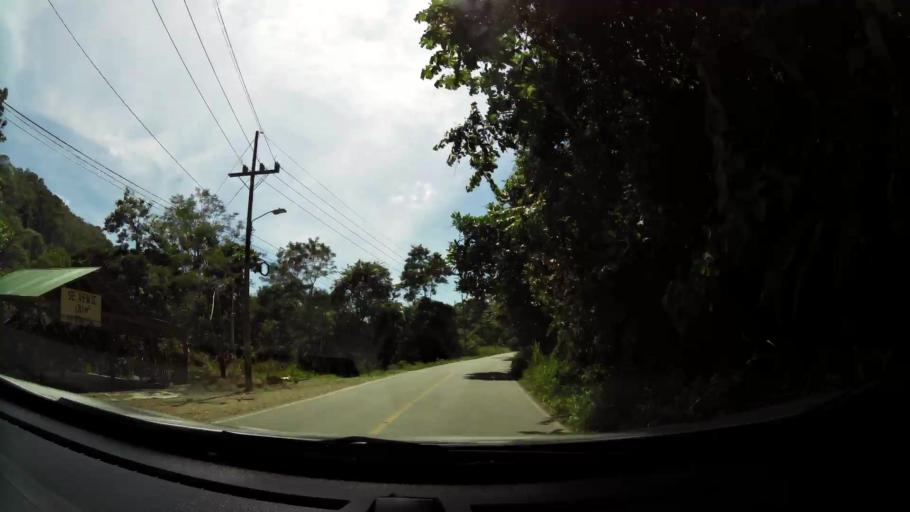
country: CR
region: San Jose
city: San Isidro
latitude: 9.2725
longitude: -83.8593
